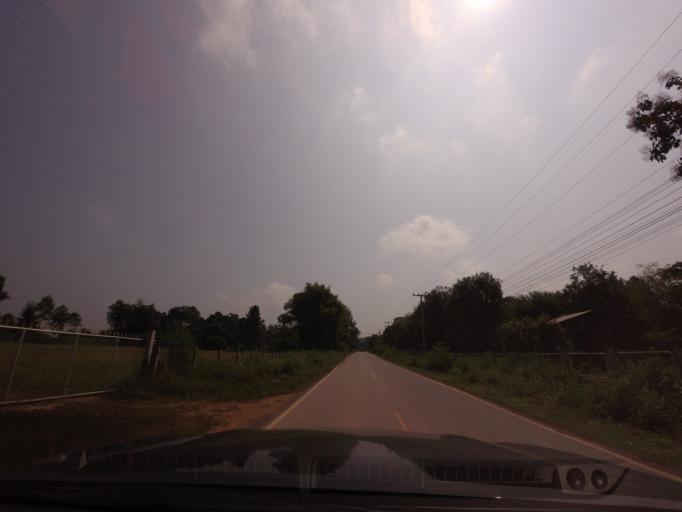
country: TH
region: Nan
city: Nan
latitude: 18.7742
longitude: 100.7402
